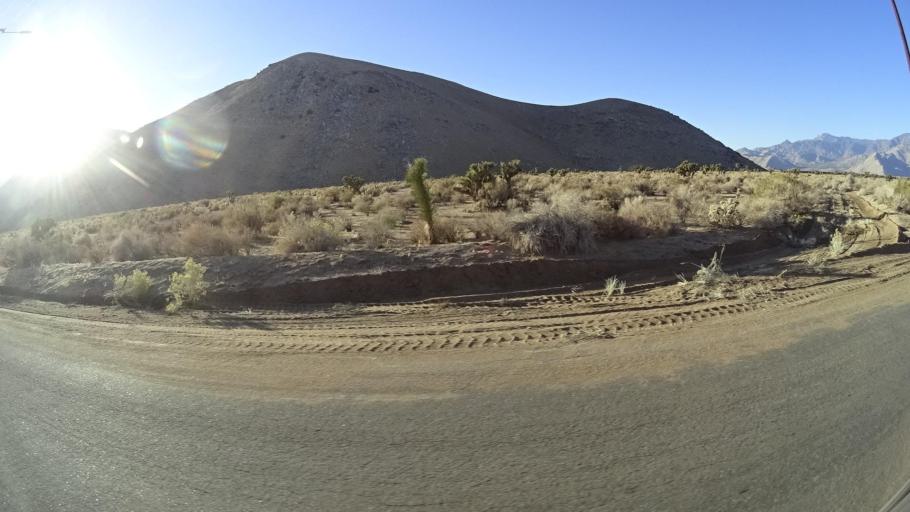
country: US
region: California
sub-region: Kern County
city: Weldon
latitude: 35.6080
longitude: -118.2425
